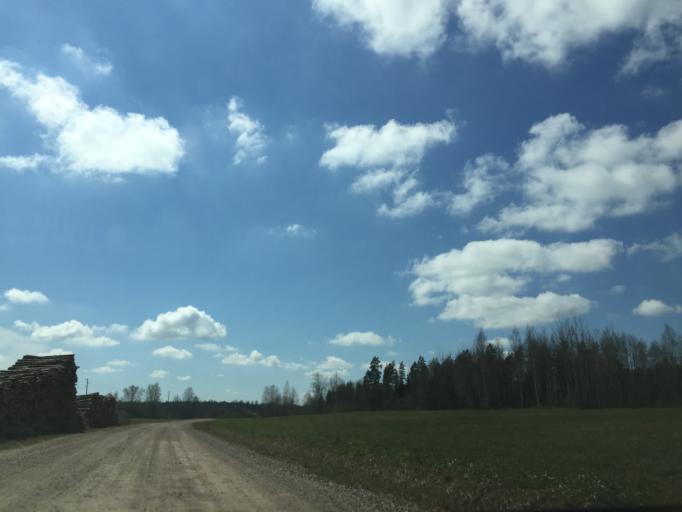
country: LV
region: Valkas Rajons
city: Valka
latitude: 57.5884
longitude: 26.0238
